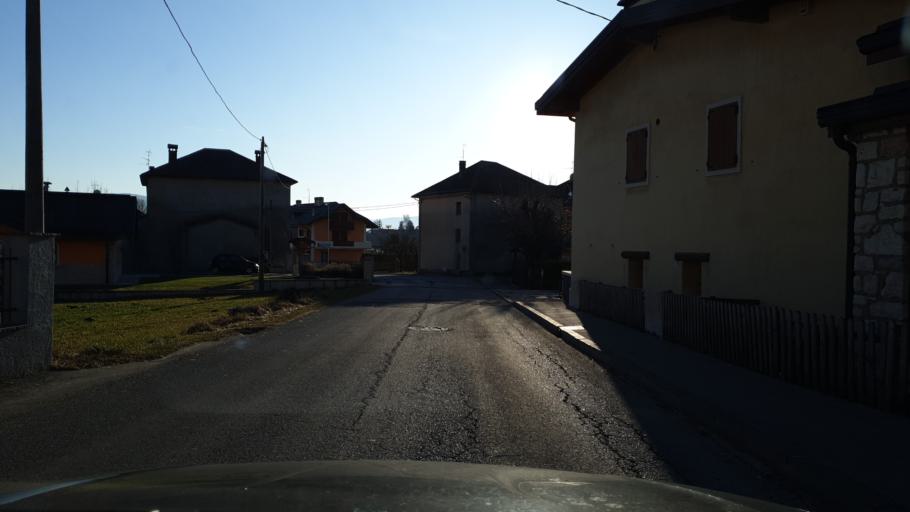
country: IT
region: Veneto
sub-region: Provincia di Vicenza
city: Asiago
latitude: 45.8846
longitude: 11.5199
